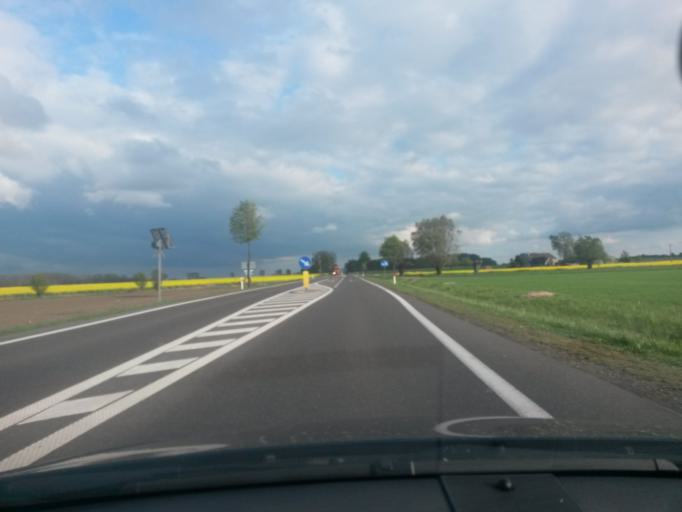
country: PL
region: Masovian Voivodeship
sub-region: Powiat plocki
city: Drobin
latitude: 52.7142
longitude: 20.0243
